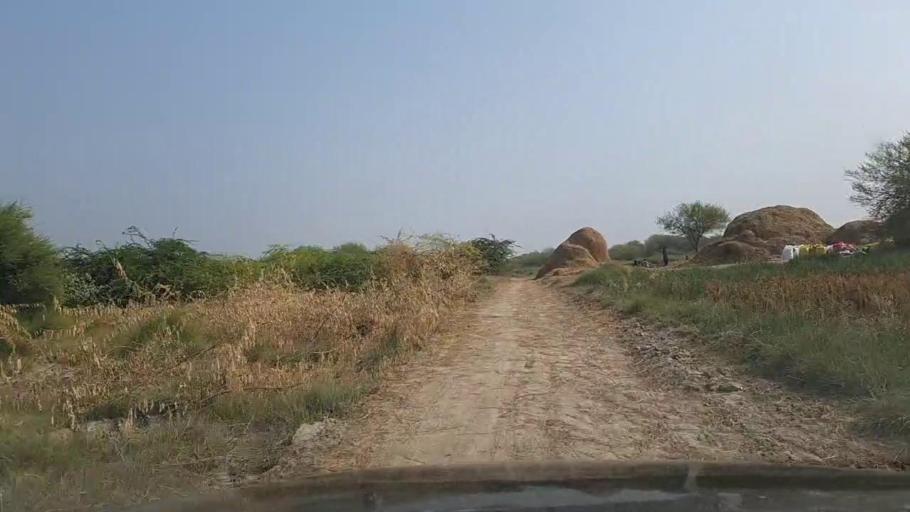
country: PK
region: Sindh
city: Mirpur Batoro
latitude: 24.6788
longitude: 68.2416
